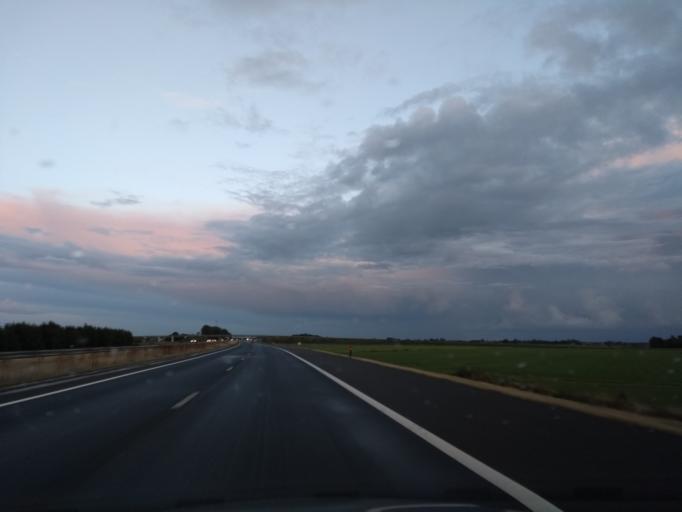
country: NL
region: Friesland
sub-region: Sudwest Fryslan
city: Oppenhuizen
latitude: 52.9895
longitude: 5.7198
